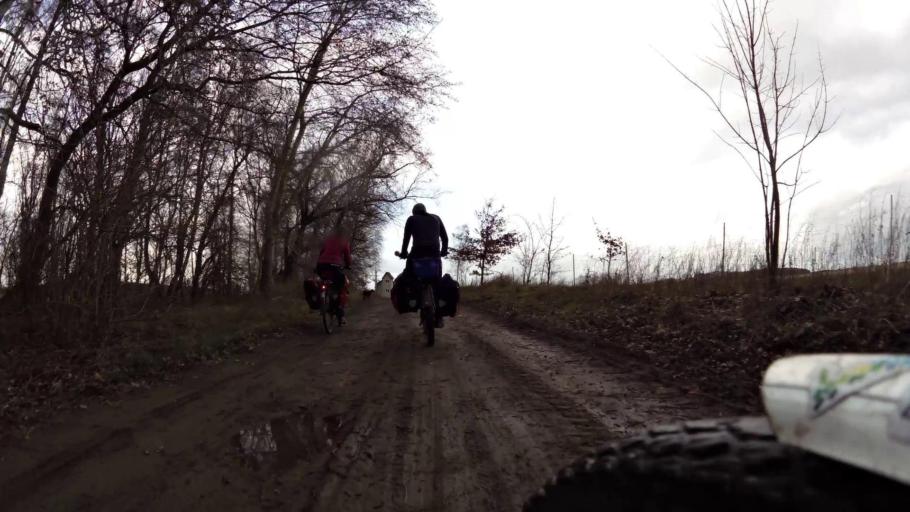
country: PL
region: West Pomeranian Voivodeship
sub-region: Powiat kamienski
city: Kamien Pomorski
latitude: 53.8865
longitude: 14.7192
